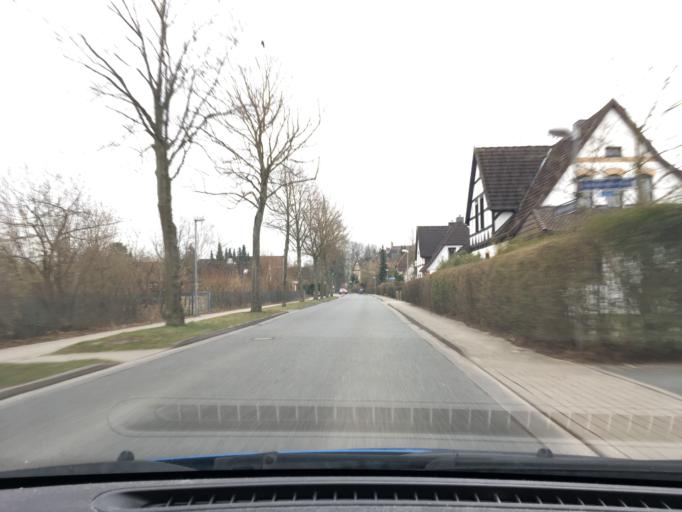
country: DE
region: Lower Saxony
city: Lueneburg
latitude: 53.2585
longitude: 10.3856
